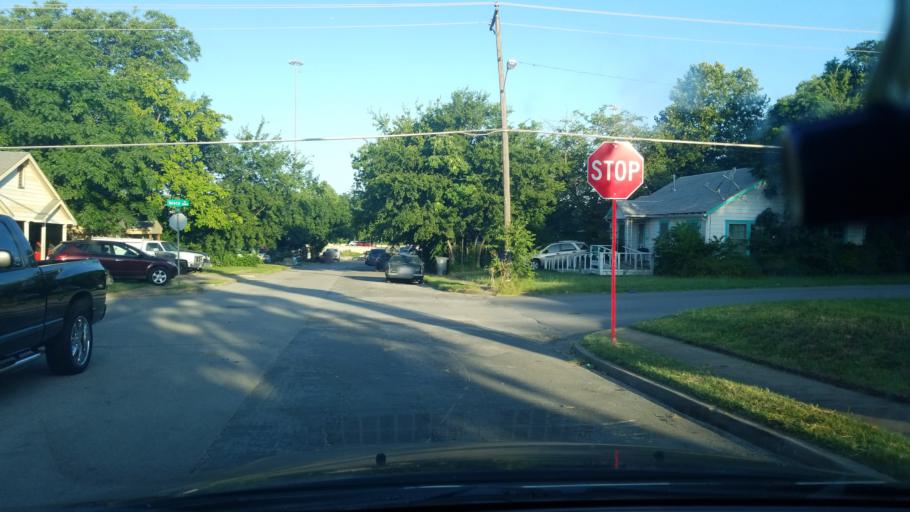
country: US
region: Texas
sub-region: Dallas County
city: Cockrell Hill
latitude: 32.7185
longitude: -96.8263
